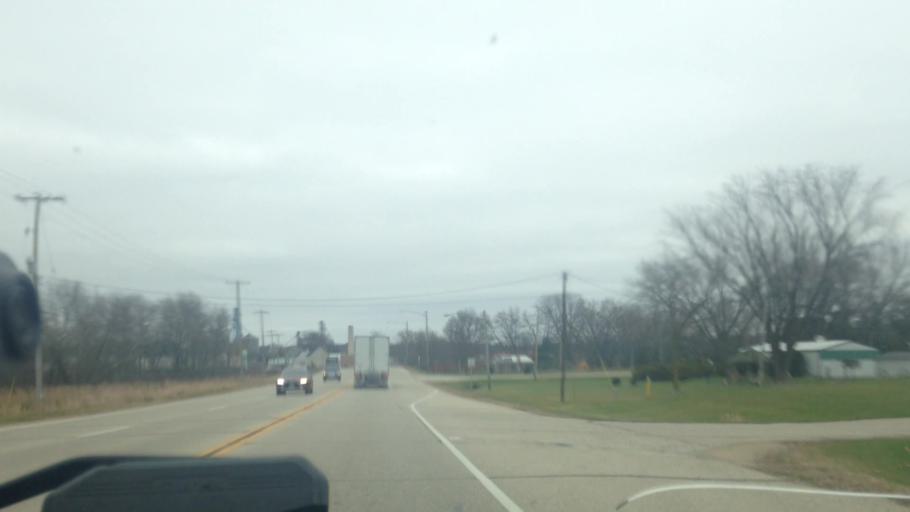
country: US
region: Wisconsin
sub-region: Washington County
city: Hartford
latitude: 43.4211
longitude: -88.3494
